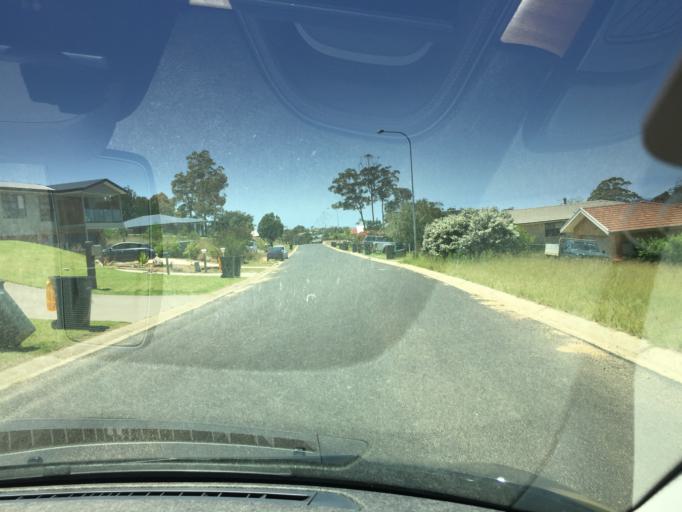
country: AU
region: New South Wales
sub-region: Bega Valley
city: Merimbula
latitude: -36.8541
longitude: 149.9272
